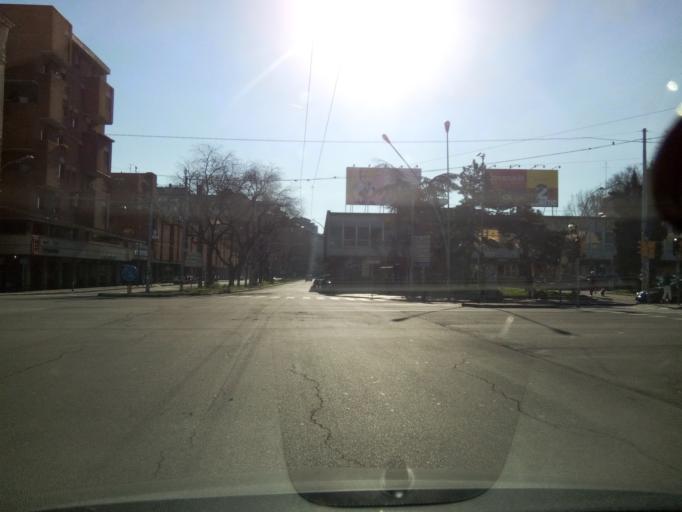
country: IT
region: Emilia-Romagna
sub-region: Provincia di Bologna
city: Bologna
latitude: 44.5048
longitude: 11.3452
